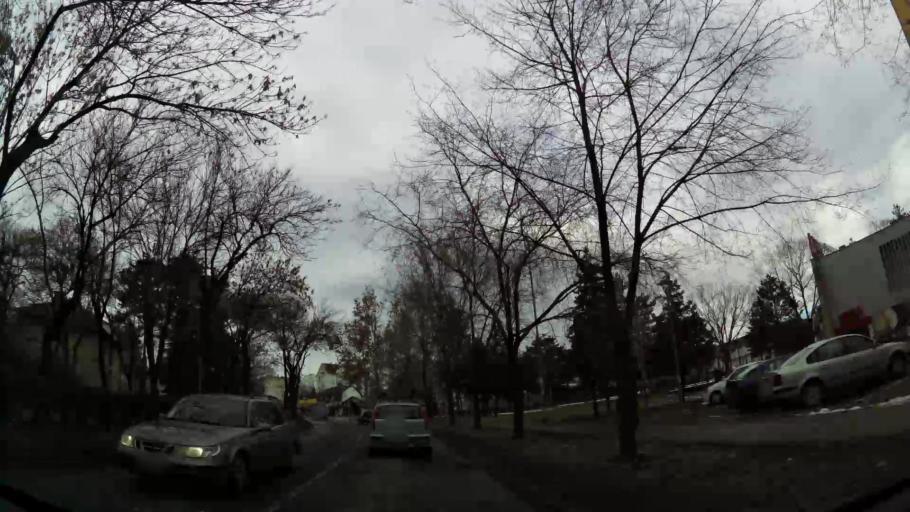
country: RS
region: Central Serbia
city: Sremcica
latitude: 44.7278
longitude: 20.3746
